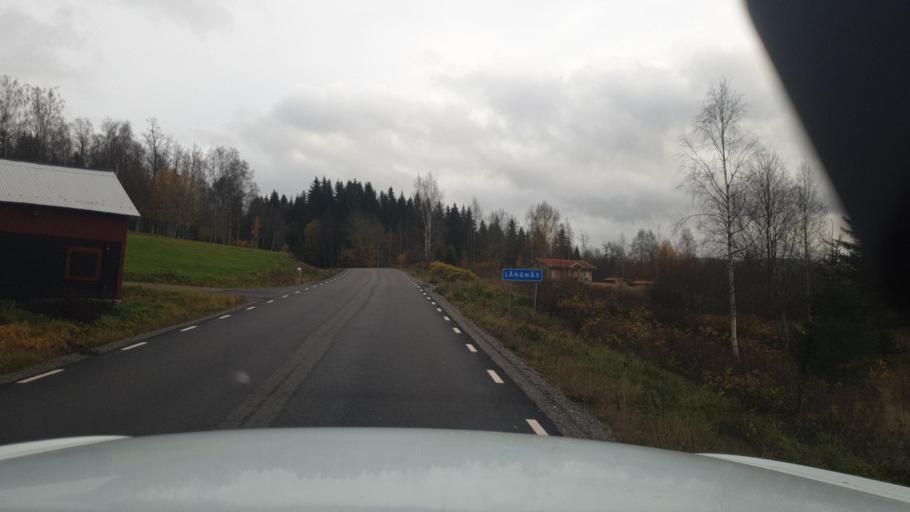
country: SE
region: Vaermland
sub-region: Torsby Kommun
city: Torsby
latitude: 59.9864
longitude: 12.7583
